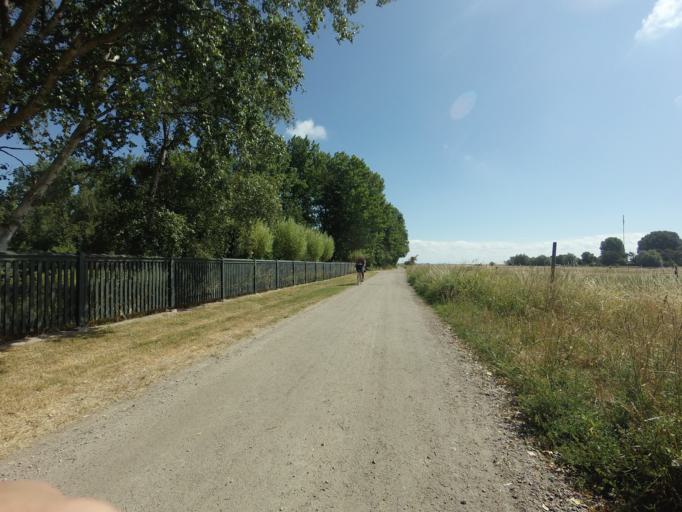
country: SE
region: Skane
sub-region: Vellinge Kommun
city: Skanor med Falsterbo
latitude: 55.4207
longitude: 12.8586
